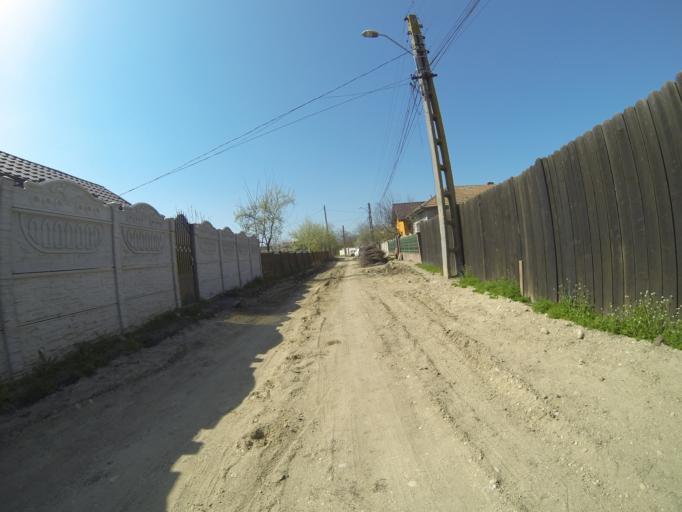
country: RO
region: Dolj
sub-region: Comuna Segarcea
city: Segarcea
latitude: 44.0944
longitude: 23.7355
